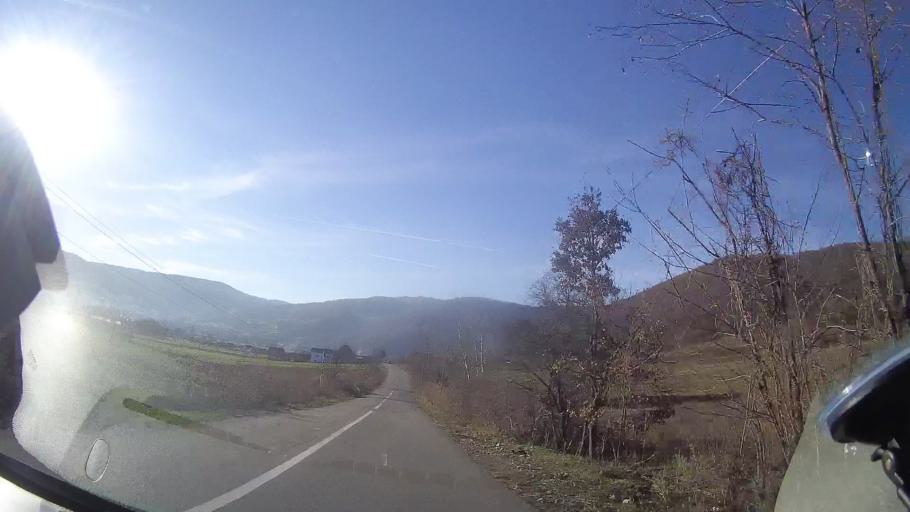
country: RO
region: Bihor
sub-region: Comuna Suncuius
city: Suncuius
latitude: 46.9586
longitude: 22.5418
